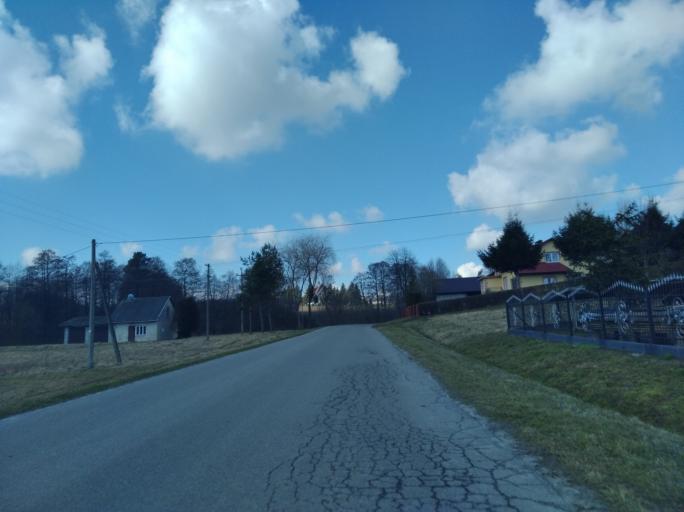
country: PL
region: Subcarpathian Voivodeship
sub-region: Powiat strzyzowski
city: Frysztak
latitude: 49.8709
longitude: 21.5299
